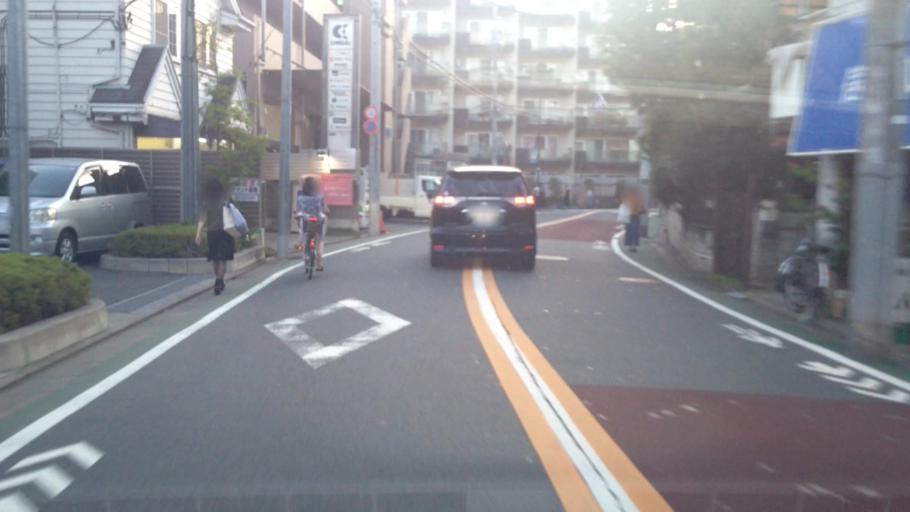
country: JP
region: Tokyo
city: Tokyo
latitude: 35.6282
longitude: 139.6909
